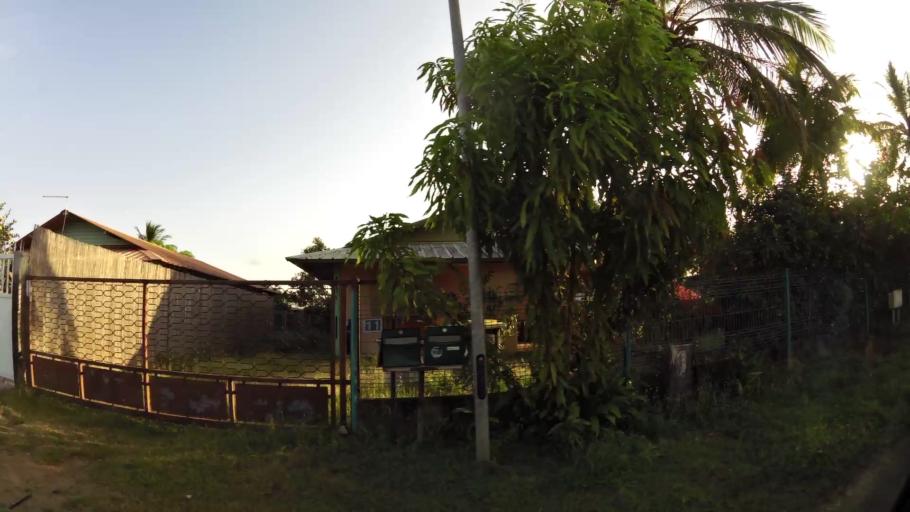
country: GF
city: Macouria
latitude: 5.0169
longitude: -52.4784
